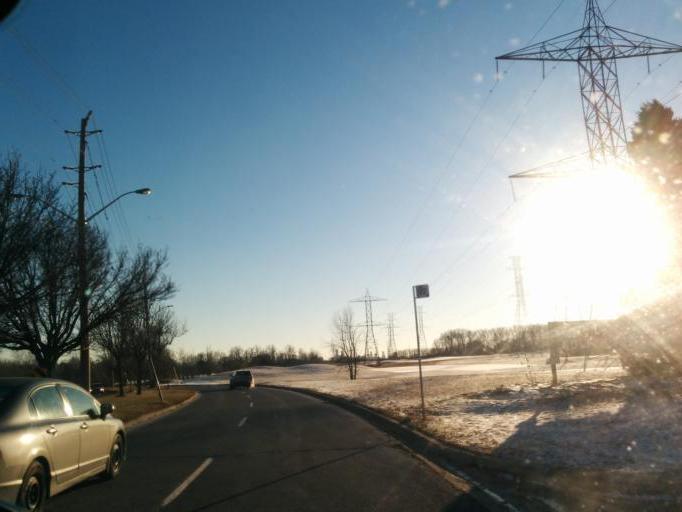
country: CA
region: Ontario
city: Etobicoke
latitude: 43.6487
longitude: -79.5966
